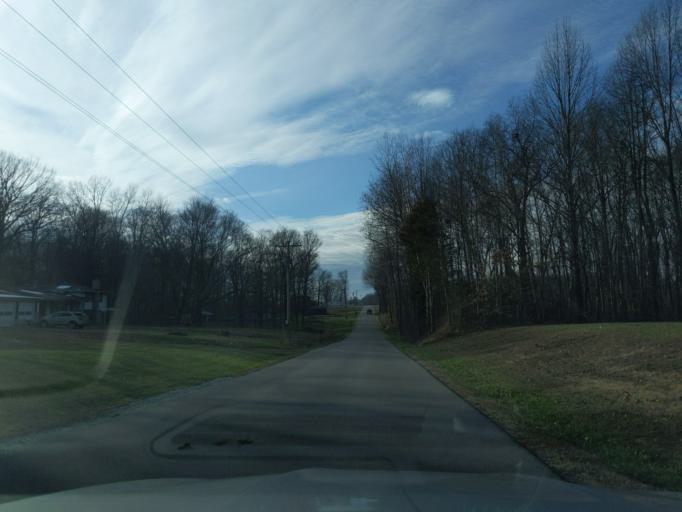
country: US
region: Indiana
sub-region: Decatur County
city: Westport
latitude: 39.1905
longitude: -85.5203
